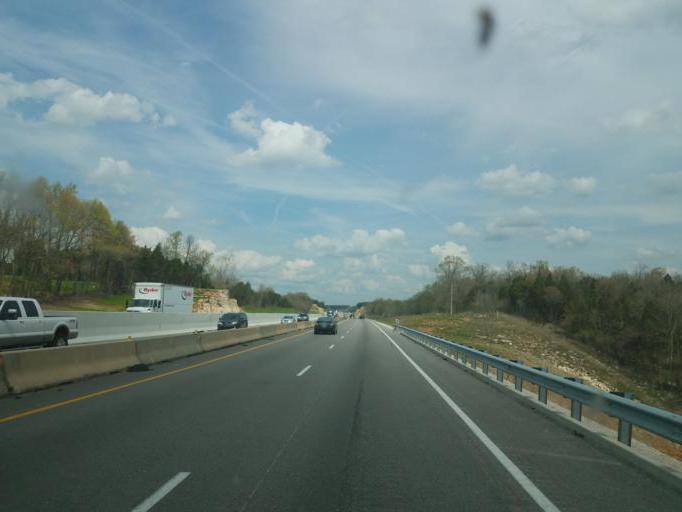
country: US
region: Kentucky
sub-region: Hart County
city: Munfordville
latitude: 37.4095
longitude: -85.8812
